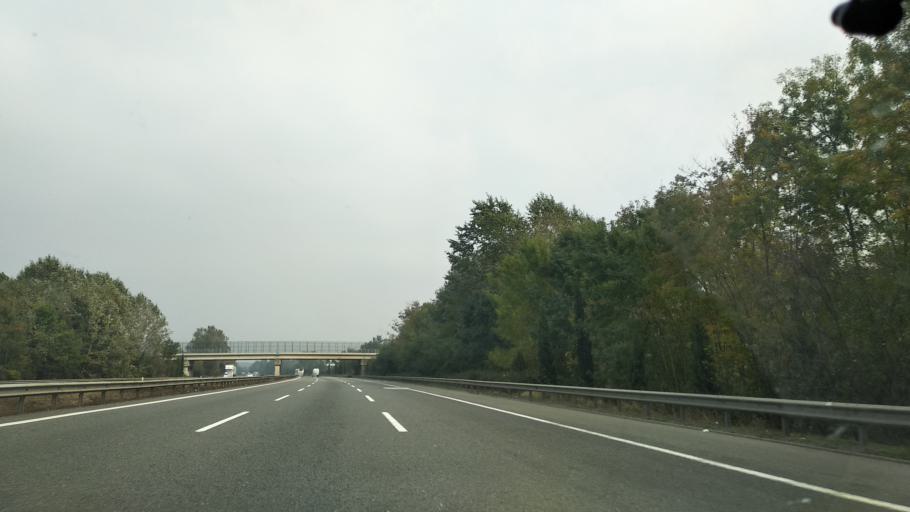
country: TR
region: Sakarya
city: Akyazi
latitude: 40.7259
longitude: 30.6281
